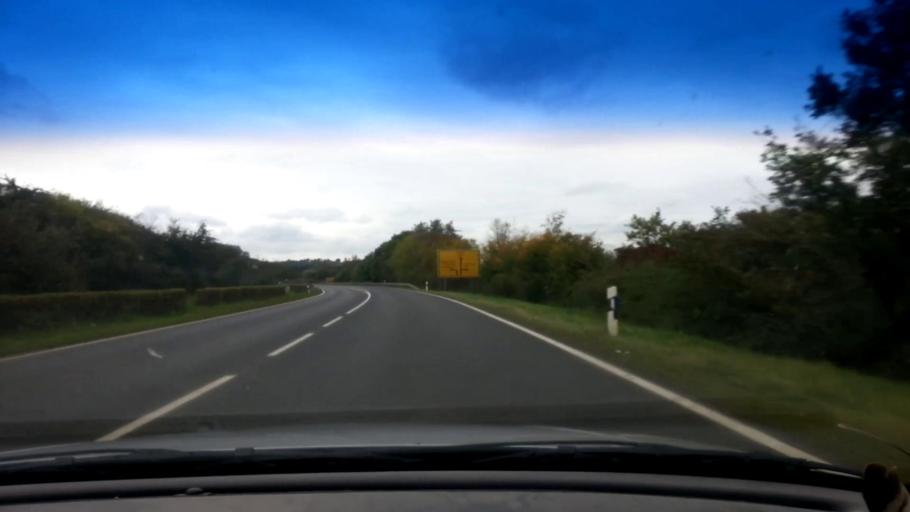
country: DE
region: Bavaria
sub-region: Upper Franconia
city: Reckendorf
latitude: 50.0025
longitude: 10.8382
